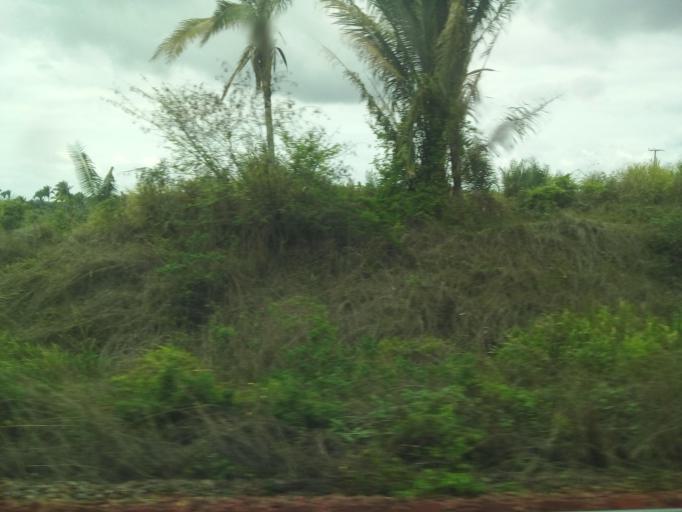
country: BR
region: Maranhao
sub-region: Santa Ines
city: Santa Ines
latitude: -3.7231
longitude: -45.5097
